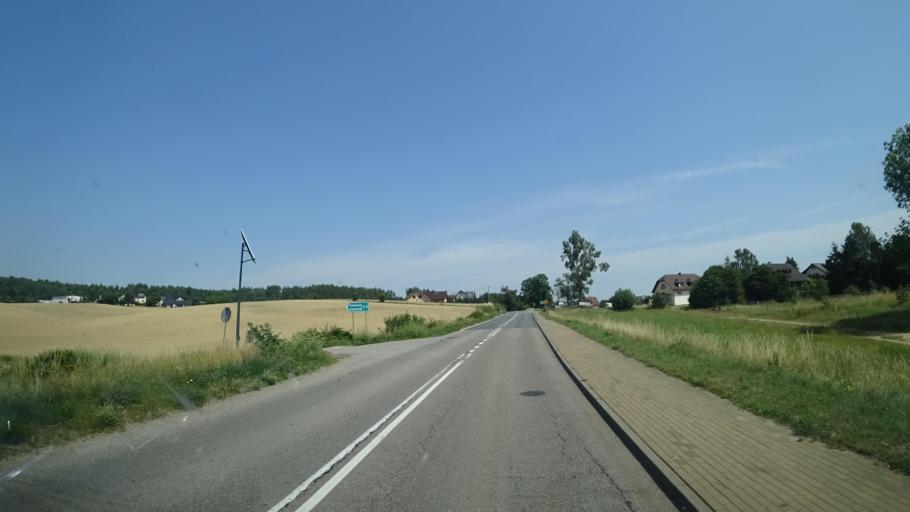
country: PL
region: Pomeranian Voivodeship
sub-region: Powiat koscierski
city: Dziemiany
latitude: 53.9729
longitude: 17.7656
